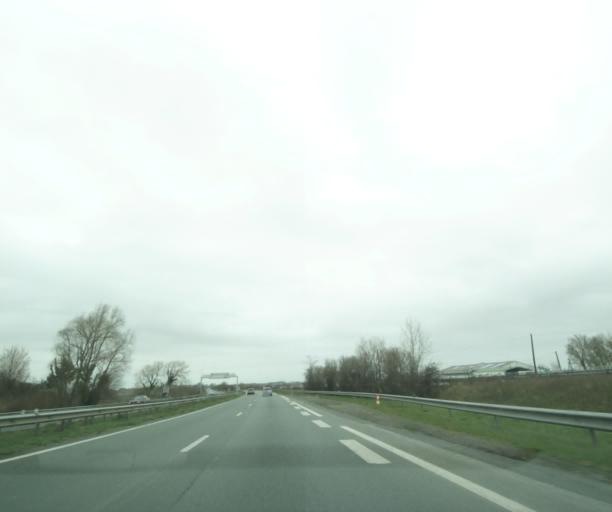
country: FR
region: Poitou-Charentes
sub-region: Departement de la Charente-Maritime
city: Breuil-Magne
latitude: 45.9720
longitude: -0.9866
